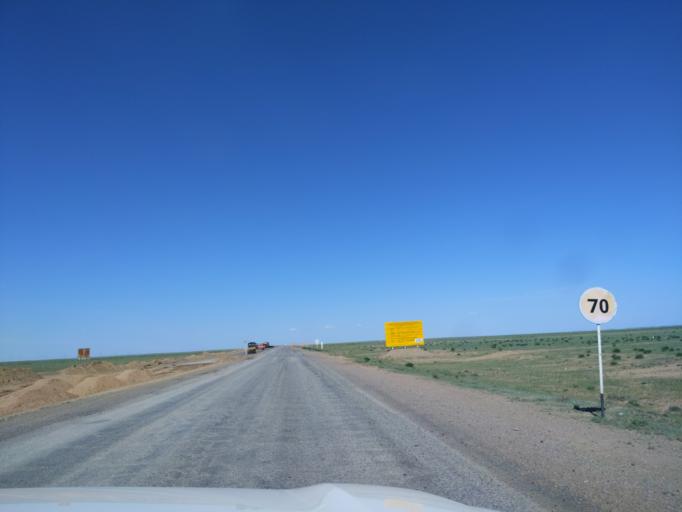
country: KZ
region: Almaty Oblysy
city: Bakanas
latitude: 44.3245
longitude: 75.4986
